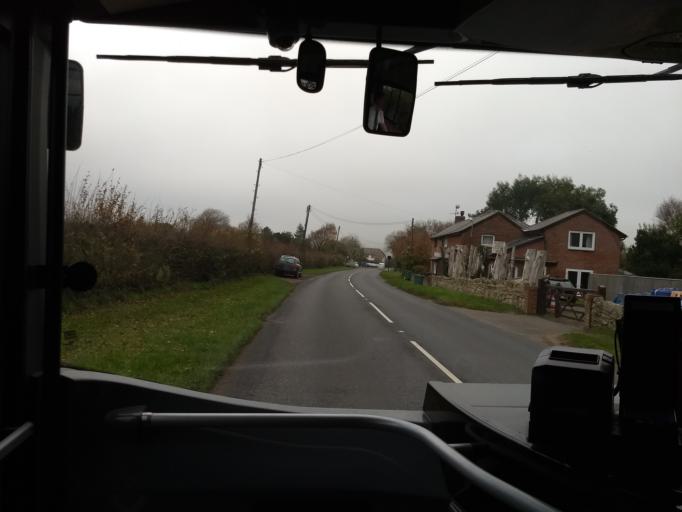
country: GB
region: England
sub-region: Isle of Wight
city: Newchurch
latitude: 50.6572
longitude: -1.2254
